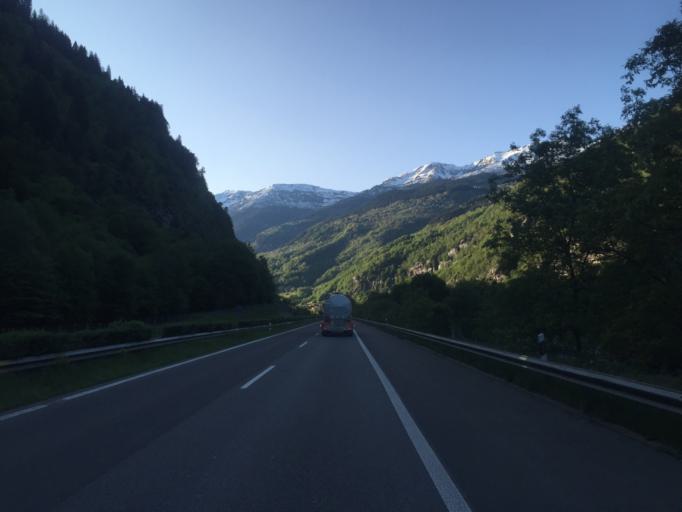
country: CH
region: Ticino
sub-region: Leventina District
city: Faido
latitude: 46.4551
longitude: 8.8270
